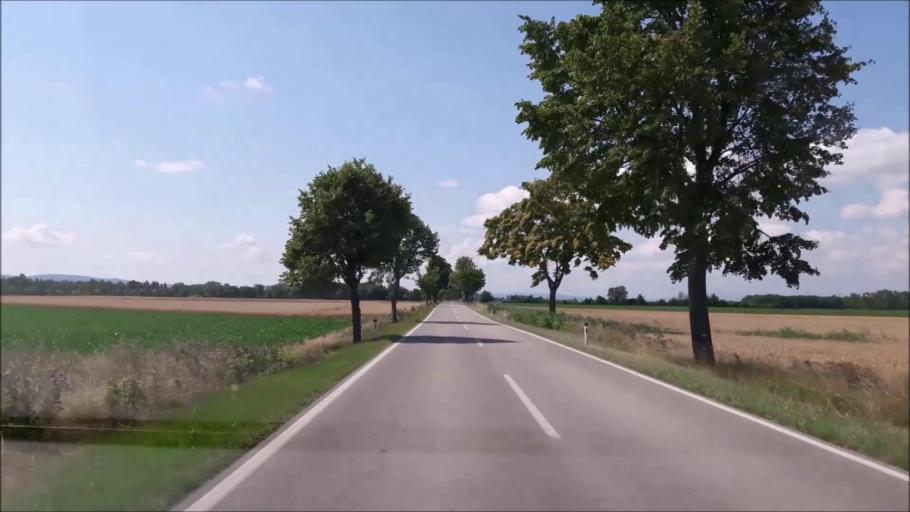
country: AT
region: Lower Austria
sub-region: Politischer Bezirk Baden
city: Mitterndorf an der Fischa
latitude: 47.9865
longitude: 16.4385
